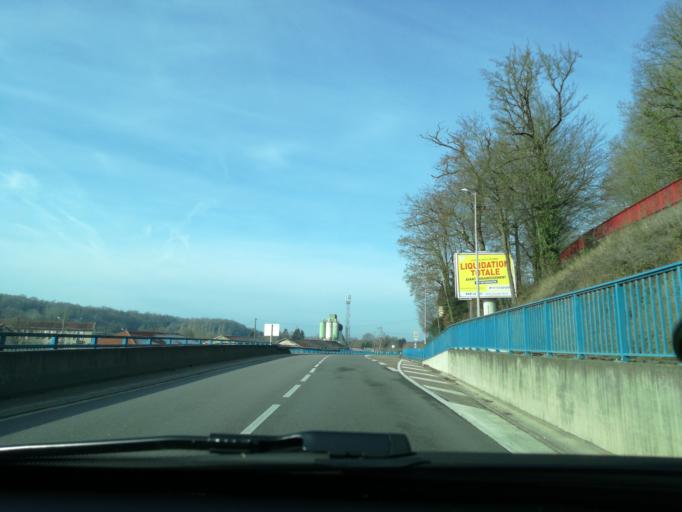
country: FR
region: Lorraine
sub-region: Departement de la Meuse
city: Bar-le-Duc
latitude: 48.7803
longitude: 5.1584
